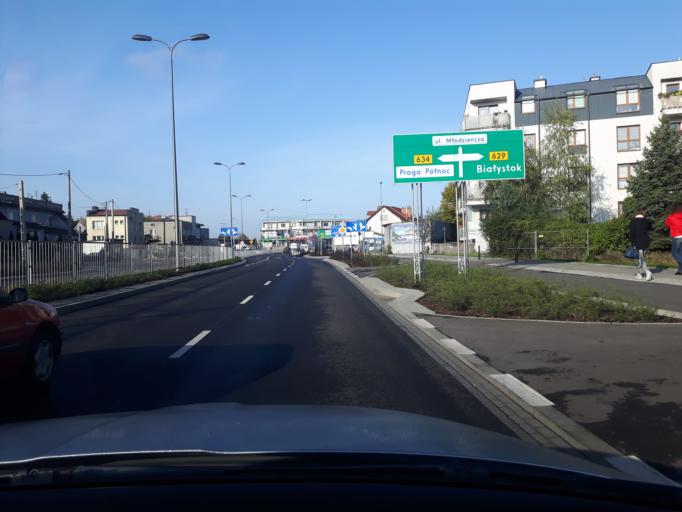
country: PL
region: Masovian Voivodeship
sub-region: Powiat wolominski
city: Zabki
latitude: 52.2868
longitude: 21.0781
